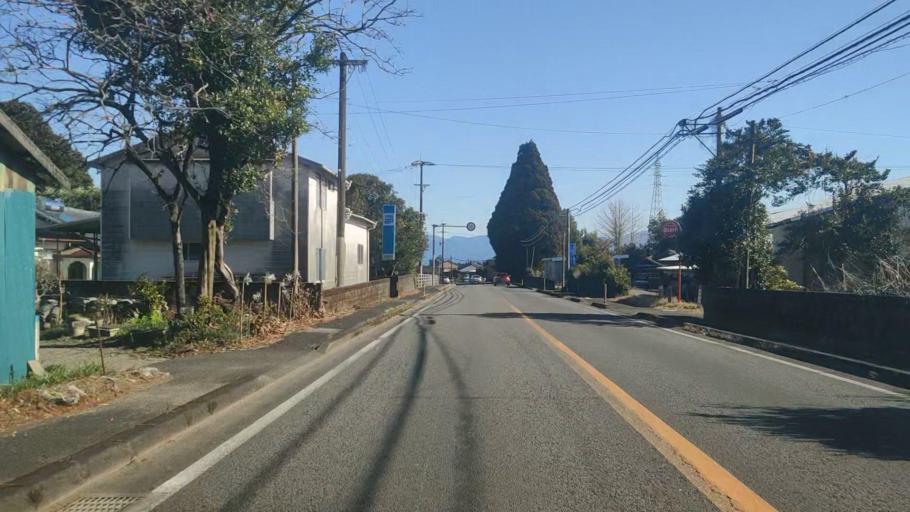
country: JP
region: Kagoshima
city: Sueyoshicho-ninokata
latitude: 31.6953
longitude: 130.9954
